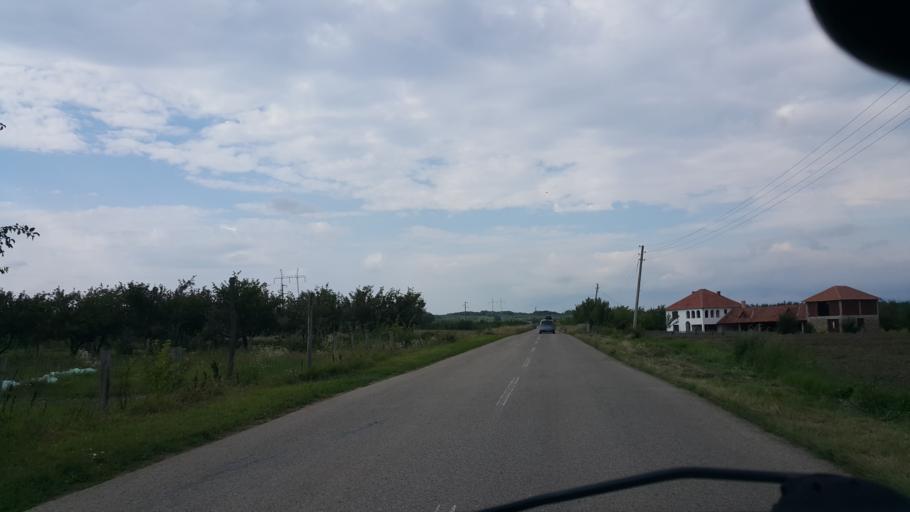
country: RS
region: Central Serbia
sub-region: Toplicki Okrug
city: Blace
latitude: 43.2391
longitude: 21.2569
